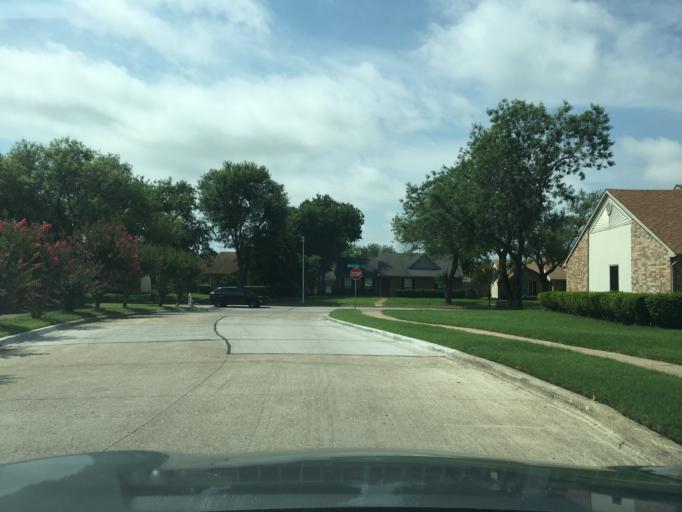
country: US
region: Texas
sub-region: Dallas County
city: Garland
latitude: 32.9238
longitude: -96.6716
